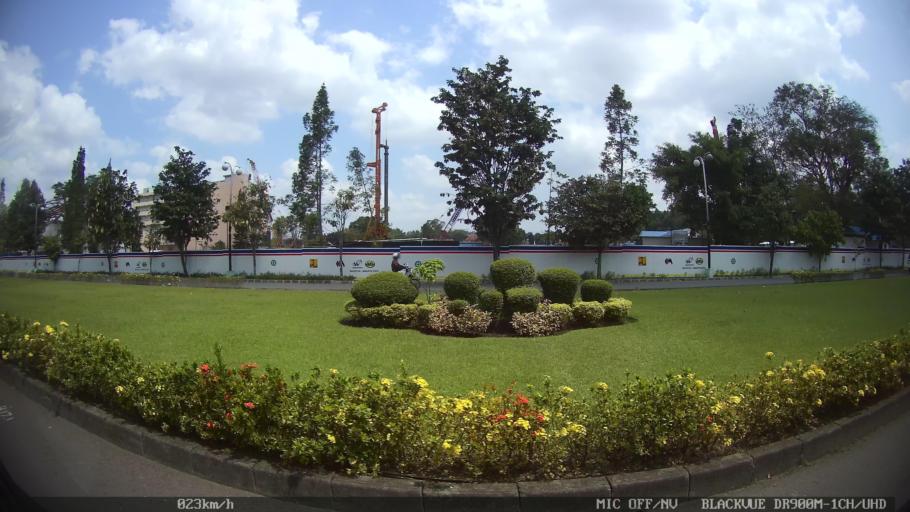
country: ID
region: Daerah Istimewa Yogyakarta
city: Yogyakarta
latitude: -7.7725
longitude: 110.3773
